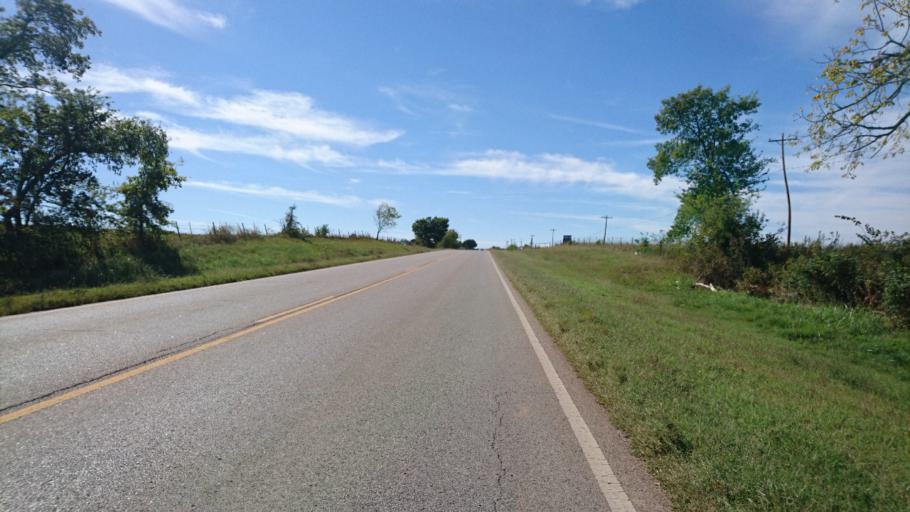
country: US
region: Oklahoma
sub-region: Lincoln County
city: Chandler
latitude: 35.7099
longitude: -96.7799
